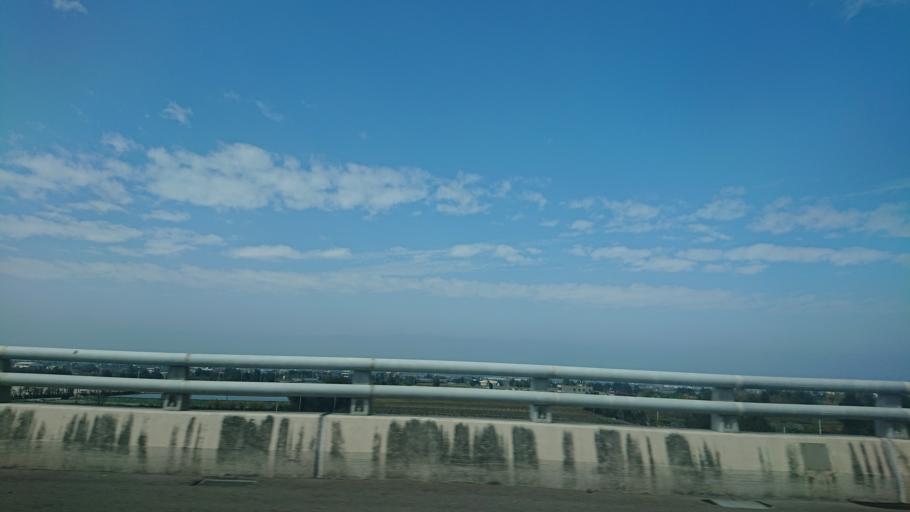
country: TW
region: Taiwan
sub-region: Yunlin
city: Douliu
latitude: 23.8488
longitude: 120.2945
